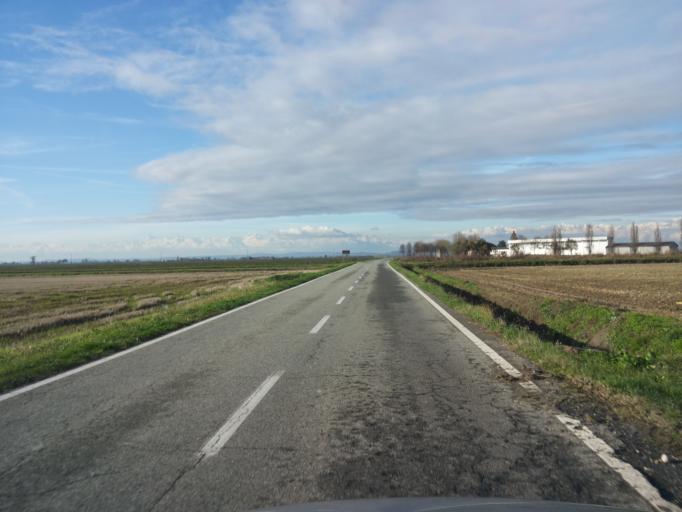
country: IT
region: Piedmont
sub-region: Provincia di Vercelli
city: Ronsecco
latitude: 45.2817
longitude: 8.2443
